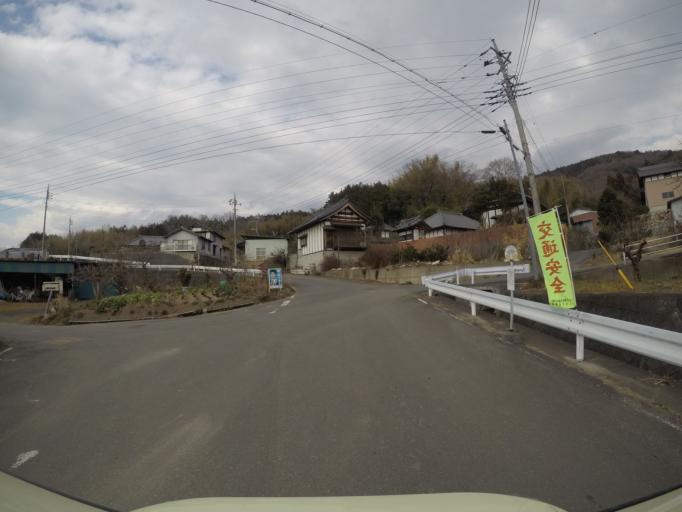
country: JP
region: Ibaraki
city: Tsukuba
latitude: 36.1704
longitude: 140.1138
